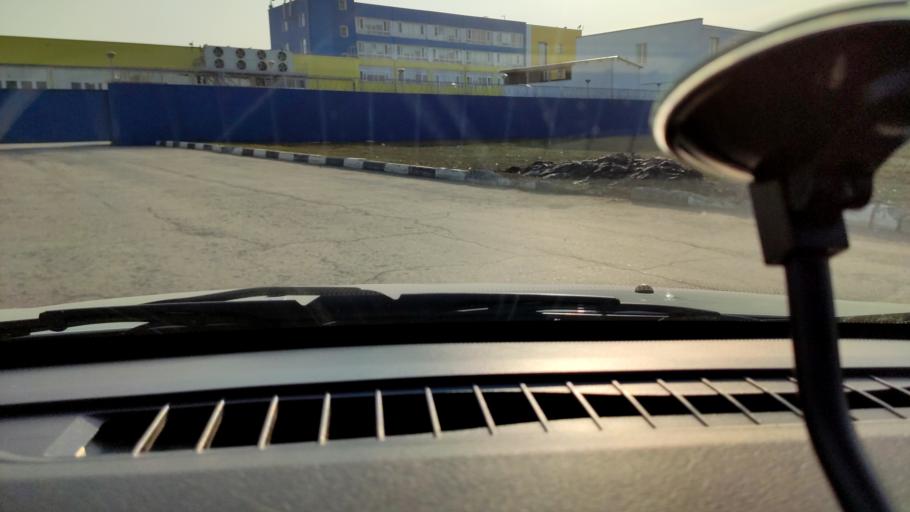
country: RU
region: Samara
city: Samara
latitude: 53.1836
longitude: 50.2625
